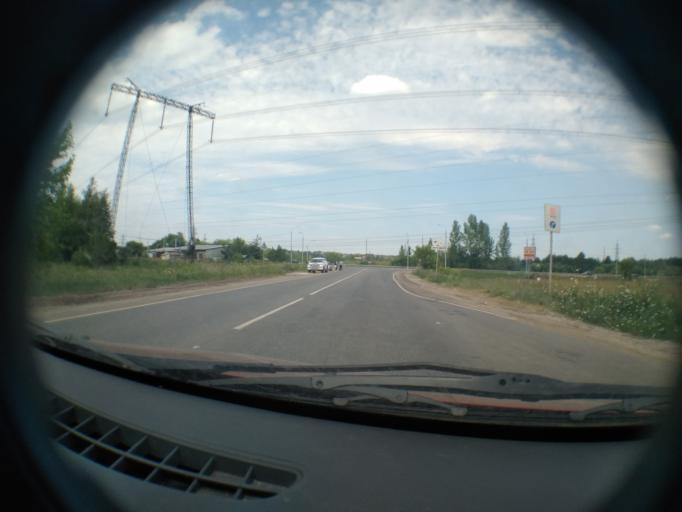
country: RU
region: Moskovskaya
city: Ostrovtsy
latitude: 55.5314
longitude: 37.9996
